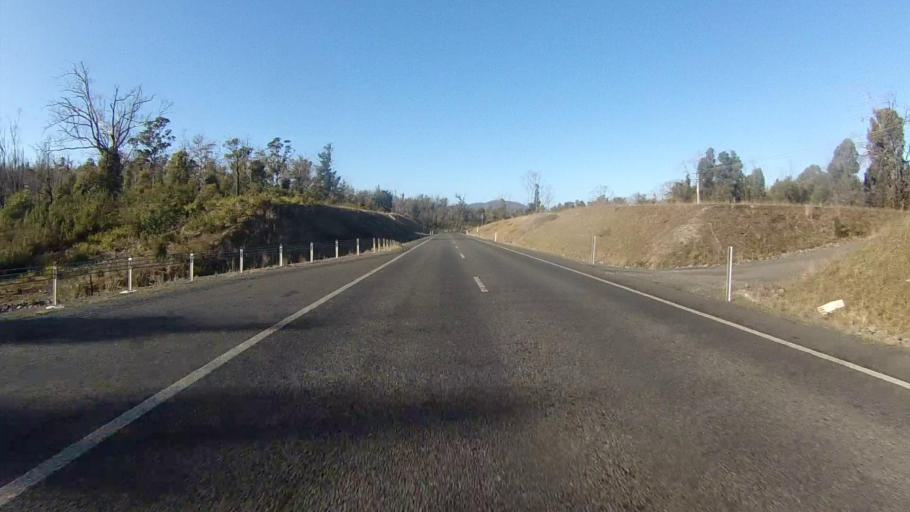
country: AU
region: Tasmania
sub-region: Sorell
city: Sorell
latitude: -42.9272
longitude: 147.8401
